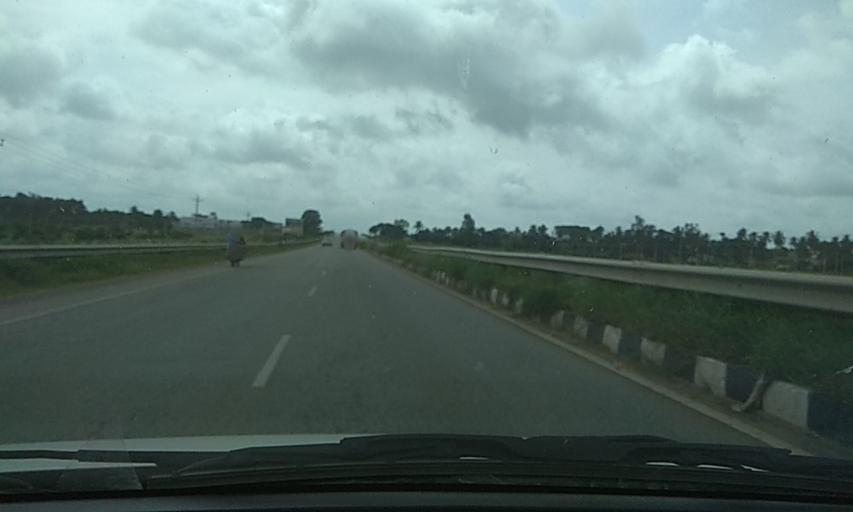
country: IN
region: Karnataka
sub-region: Davanagere
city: Harihar
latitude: 14.4571
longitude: 75.8633
